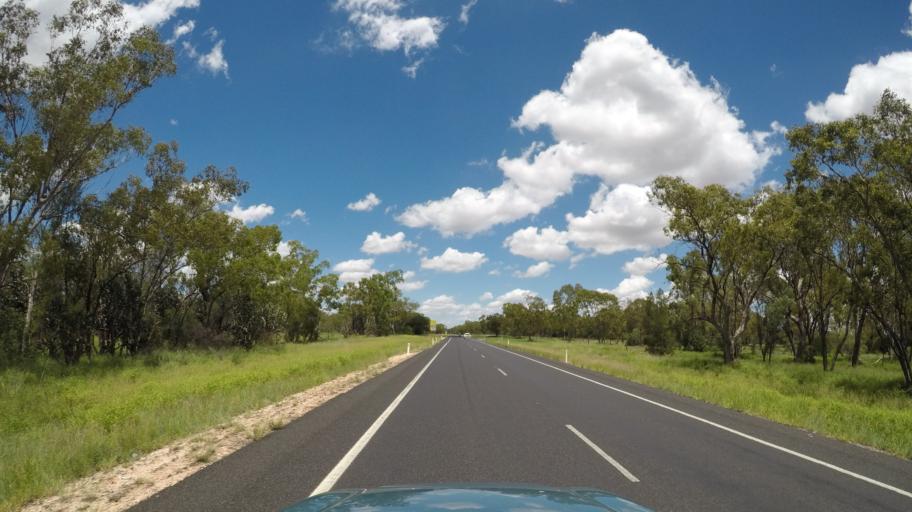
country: AU
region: Queensland
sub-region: Goondiwindi
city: Goondiwindi
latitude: -28.0758
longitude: 150.7452
